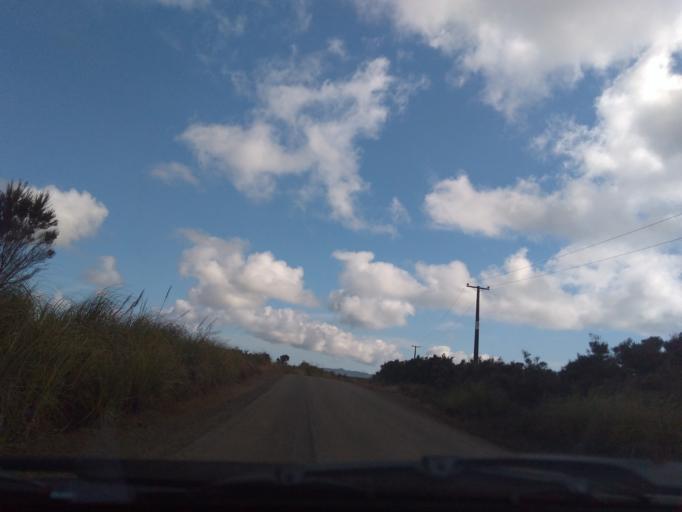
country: NZ
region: Northland
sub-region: Far North District
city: Taipa
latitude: -34.9524
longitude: 173.3737
